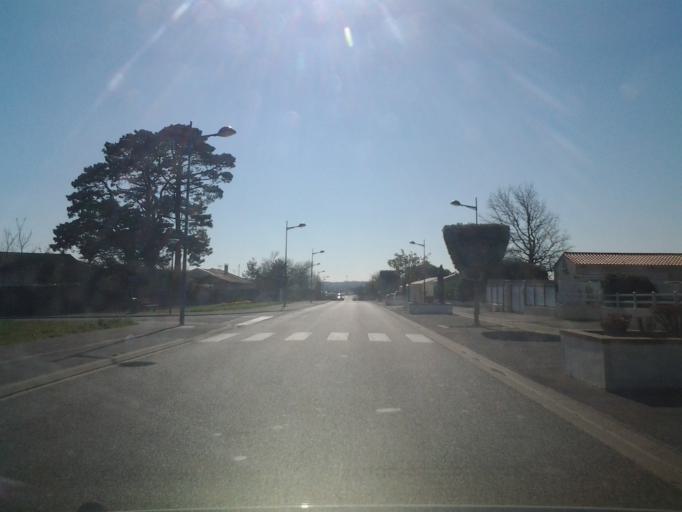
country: FR
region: Pays de la Loire
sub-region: Departement de la Vendee
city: Saint-Mathurin
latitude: 46.5619
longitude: -1.7172
